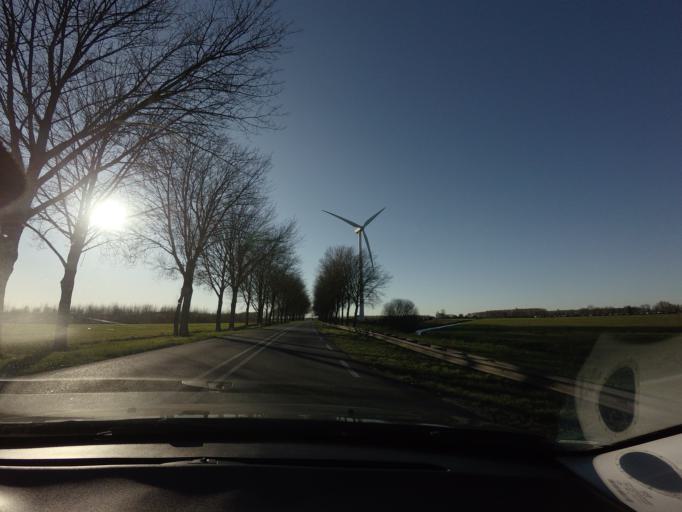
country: NL
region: Gelderland
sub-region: Gemeente Culemborg
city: Culemborg
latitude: 51.9349
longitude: 5.1952
